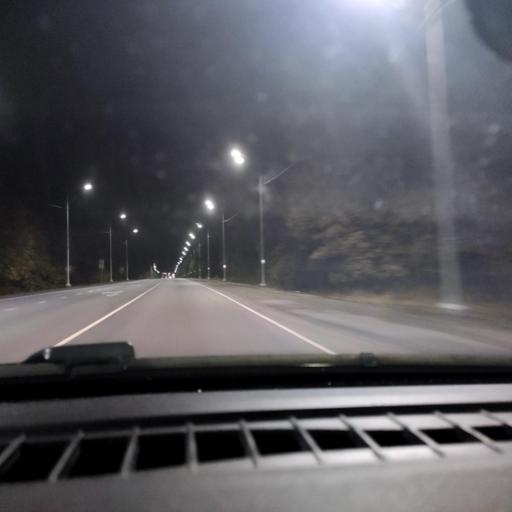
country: RU
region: Voronezj
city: Semiluki
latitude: 51.6489
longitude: 39.0292
